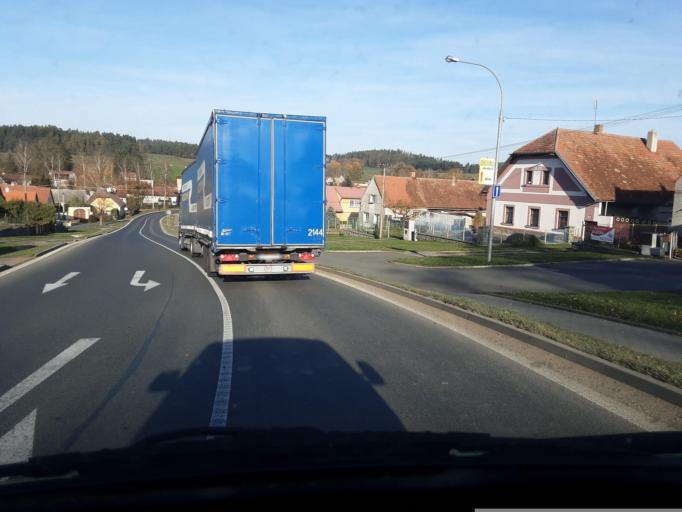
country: CZ
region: Plzensky
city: Horazd'ovice
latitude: 49.3293
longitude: 13.6475
